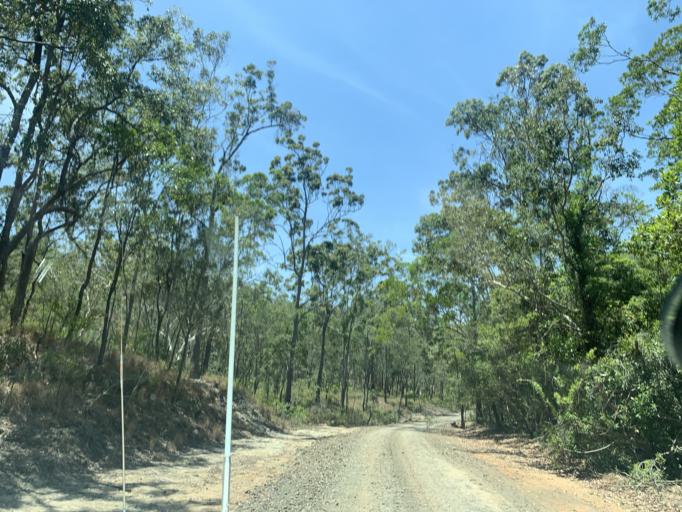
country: AU
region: Queensland
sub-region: Cairns
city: Redlynch
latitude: -16.9301
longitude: 145.6019
